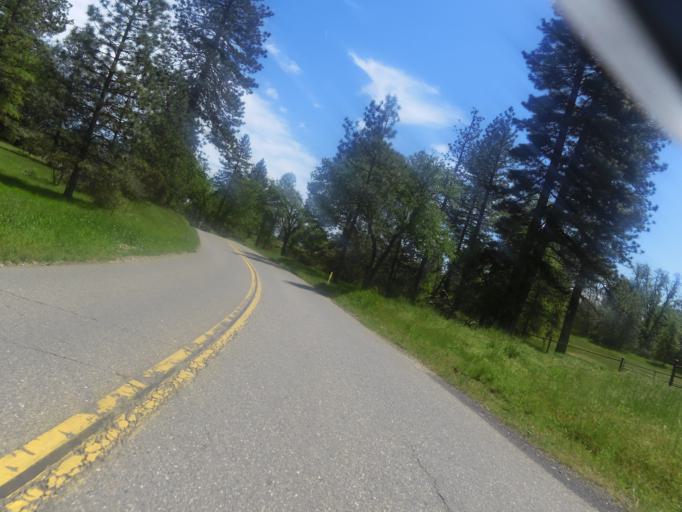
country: US
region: California
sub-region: Mariposa County
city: Midpines
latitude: 37.5123
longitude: -119.8284
